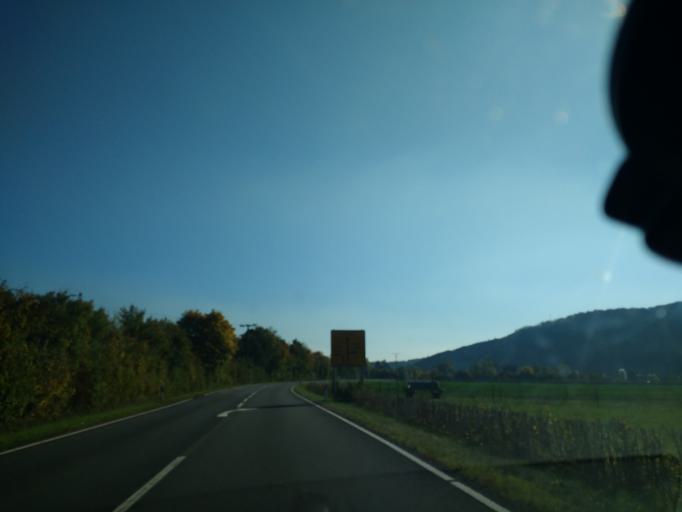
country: DE
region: Rheinland-Pfalz
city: Kanzem
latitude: 49.6686
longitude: 6.5599
